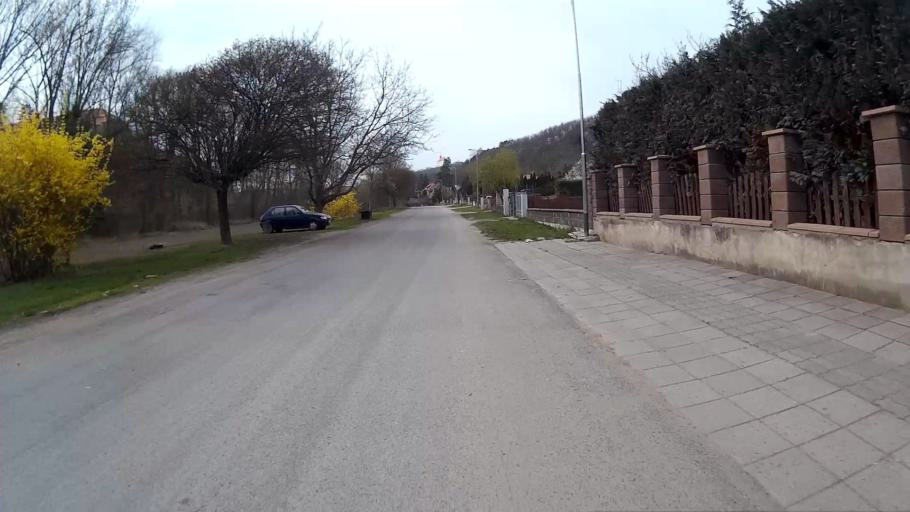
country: CZ
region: South Moravian
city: Dolni Kounice
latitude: 49.0665
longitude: 16.4764
